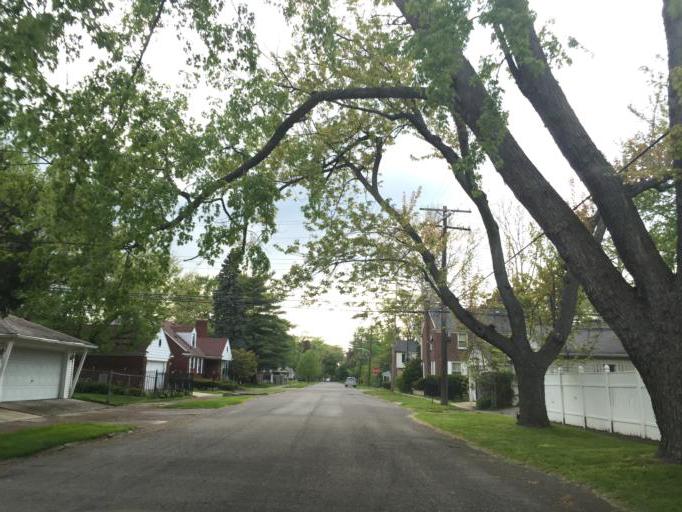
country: US
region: Michigan
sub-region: Oakland County
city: Southfield
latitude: 42.4118
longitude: -83.2243
